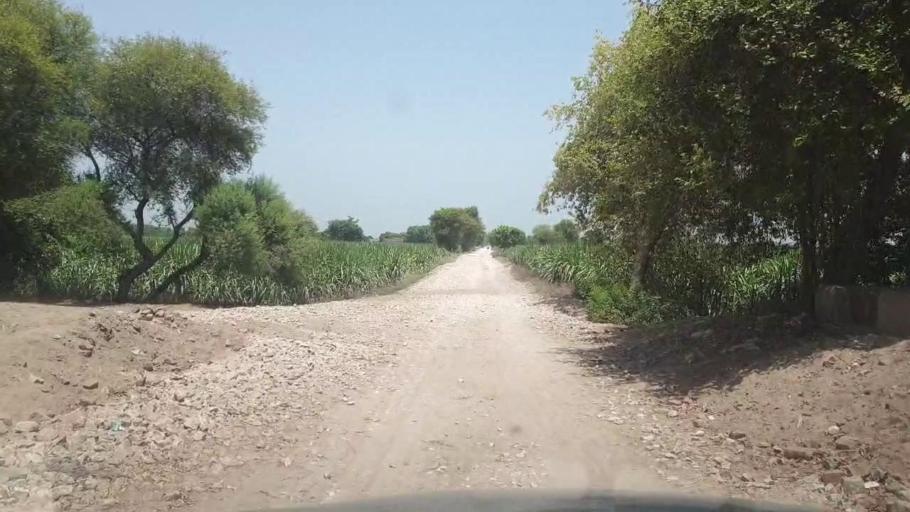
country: PK
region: Sindh
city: Sobhadero
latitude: 27.3242
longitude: 68.3495
